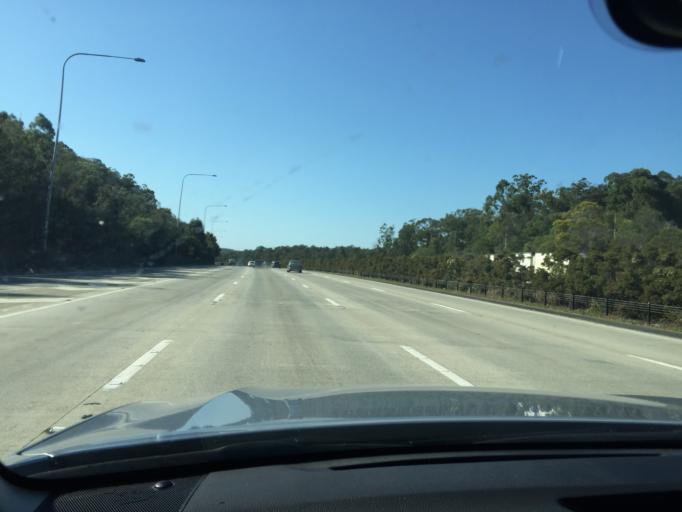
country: AU
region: Queensland
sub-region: Gold Coast
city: Ormeau Hills
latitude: -27.8067
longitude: 153.2664
